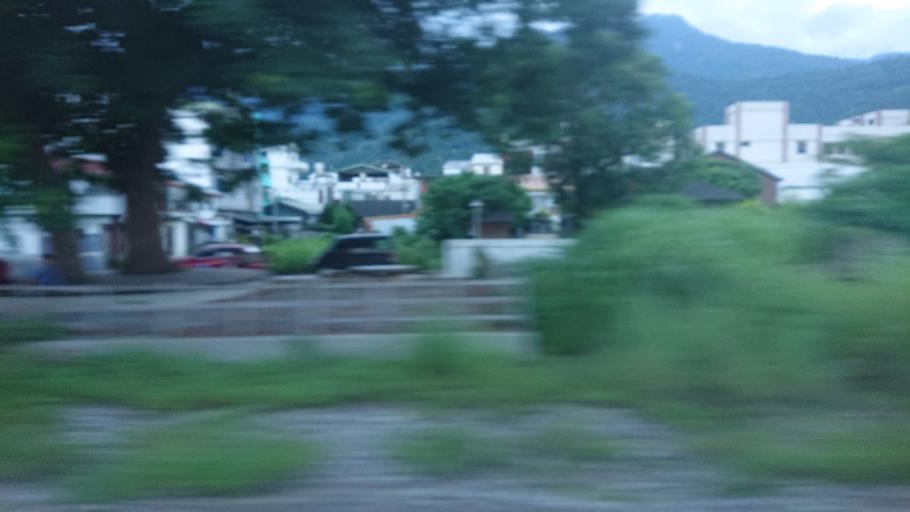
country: TW
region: Taiwan
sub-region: Taitung
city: Taitung
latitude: 23.0471
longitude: 121.1650
